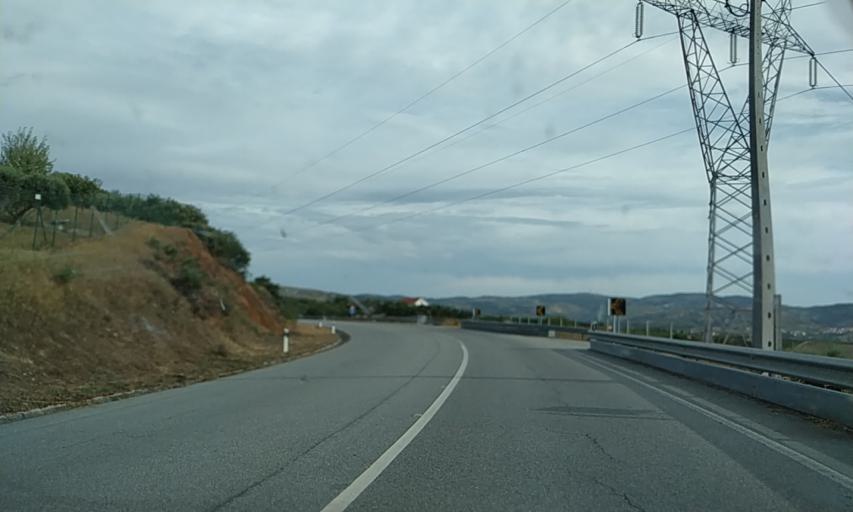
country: PT
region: Viseu
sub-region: Sao Joao da Pesqueira
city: Sao Joao da Pesqueira
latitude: 41.1122
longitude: -7.3893
